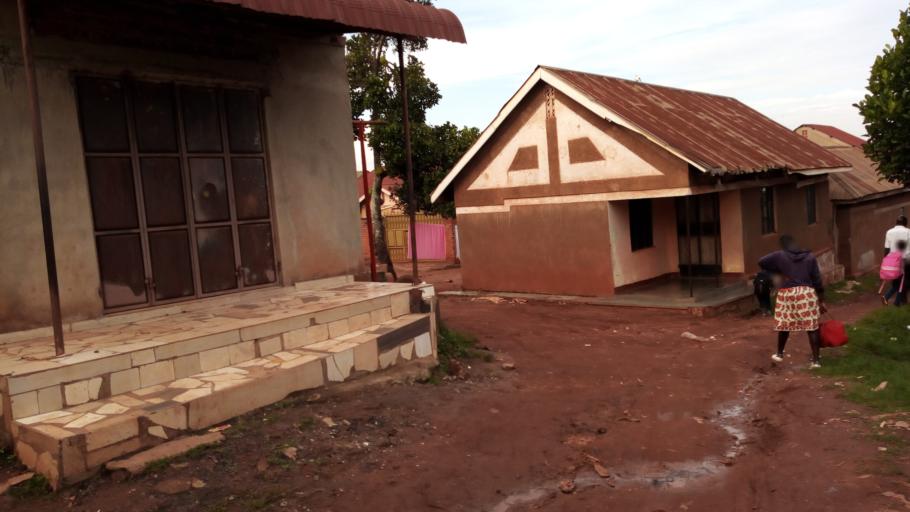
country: UG
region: Central Region
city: Kampala Central Division
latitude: 0.3720
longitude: 32.5536
